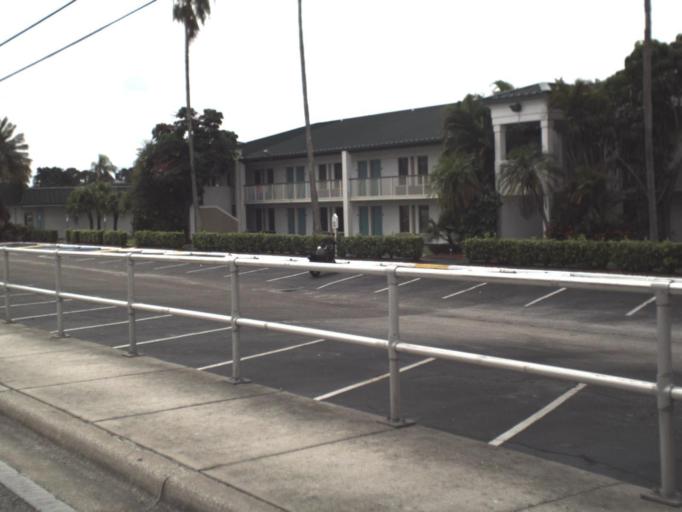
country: US
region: Florida
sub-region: Manatee County
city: Whitfield
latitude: 27.4142
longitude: -82.5735
